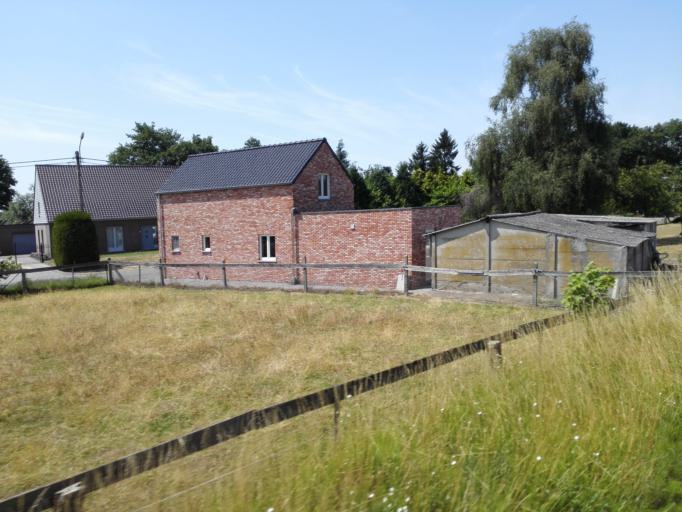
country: BE
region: Flanders
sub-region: Provincie Antwerpen
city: Heist-op-den-Berg
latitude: 51.0489
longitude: 4.7530
